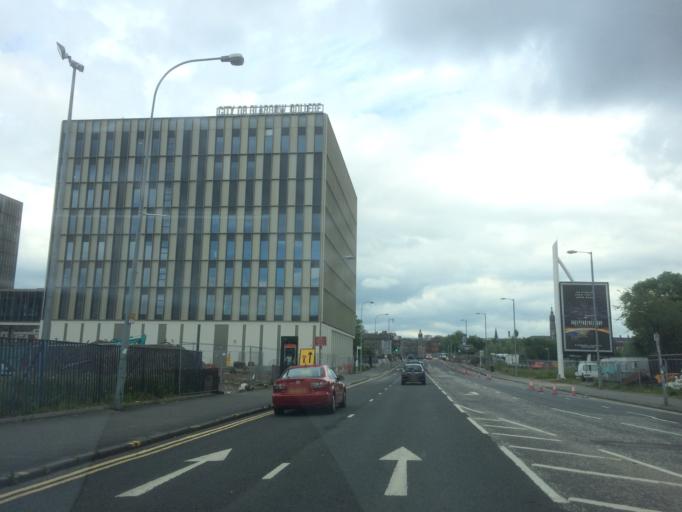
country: GB
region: Scotland
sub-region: Glasgow City
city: Glasgow
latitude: 55.8509
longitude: -4.2488
